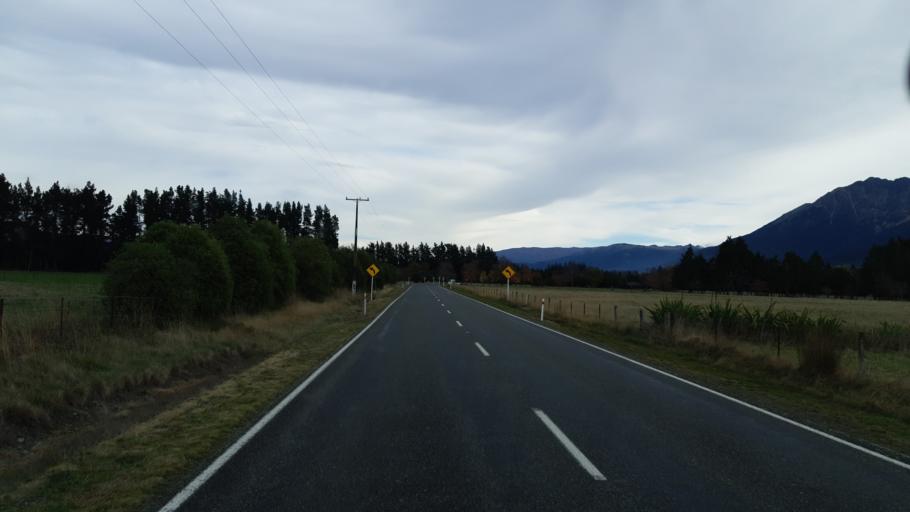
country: NZ
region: Tasman
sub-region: Tasman District
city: Brightwater
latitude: -41.6281
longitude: 173.3382
